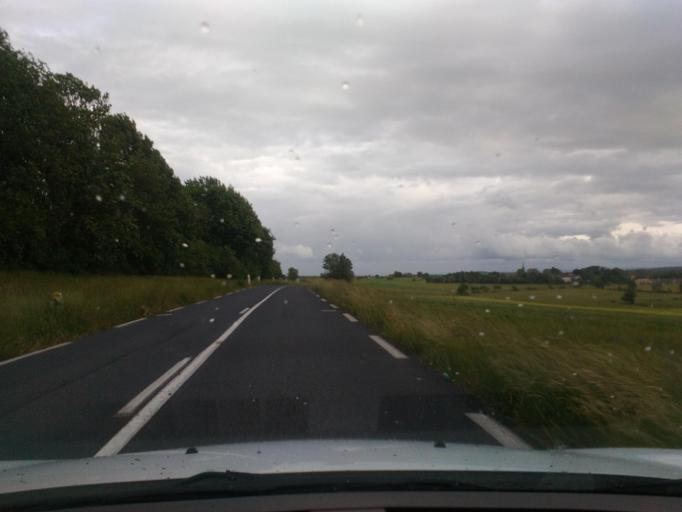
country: FR
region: Lorraine
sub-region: Departement de Meurthe-et-Moselle
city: Gerbeviller
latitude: 48.4583
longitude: 6.5593
